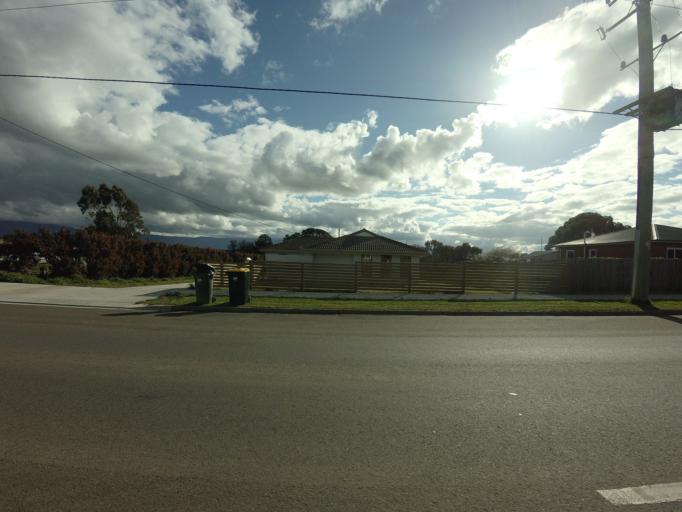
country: AU
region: Tasmania
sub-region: Northern Midlands
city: Longford
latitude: -41.6937
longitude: 147.0786
